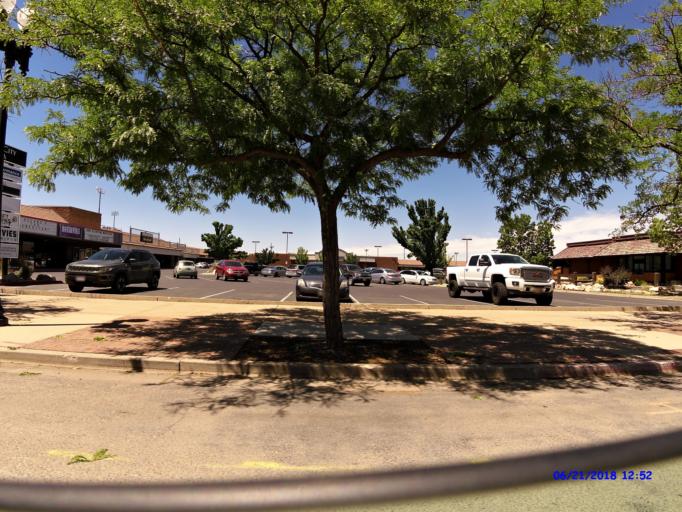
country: US
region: Utah
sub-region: Weber County
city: Ogden
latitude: 41.2257
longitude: -111.9732
